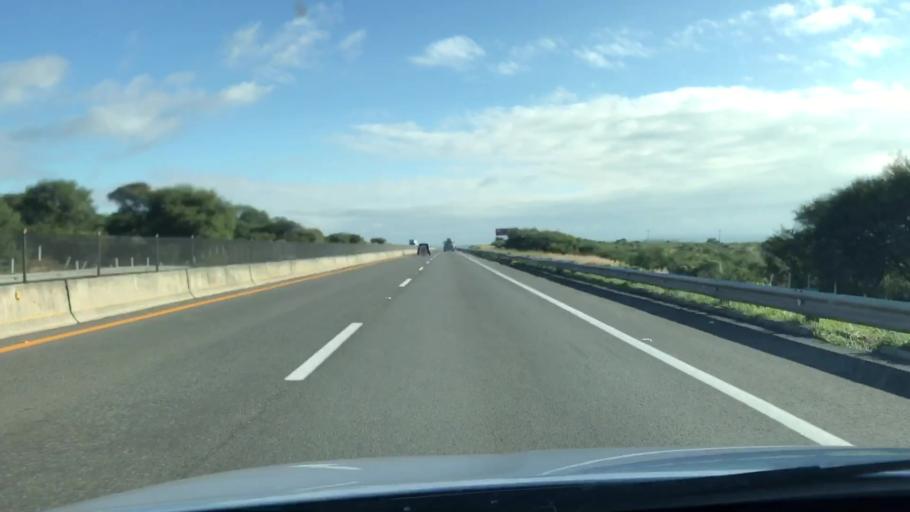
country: MX
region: Jalisco
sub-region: San Juan de los Lagos
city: Mezquitic de la Magdalena
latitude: 21.2102
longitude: -102.3271
